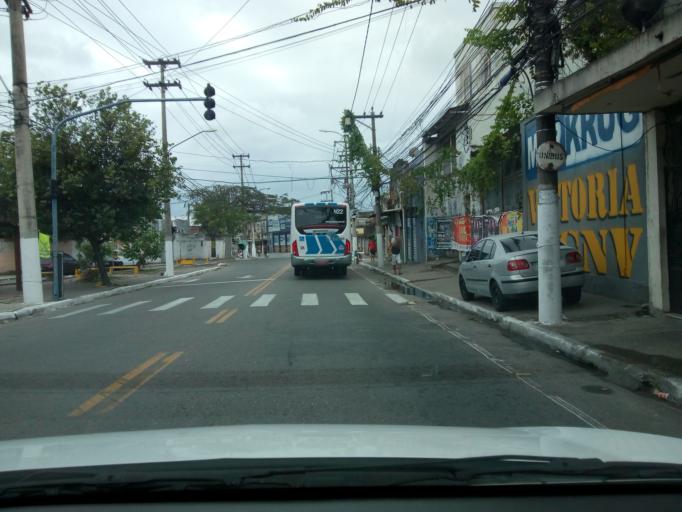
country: BR
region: Rio de Janeiro
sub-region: Niteroi
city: Niteroi
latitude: -22.8657
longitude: -43.1036
